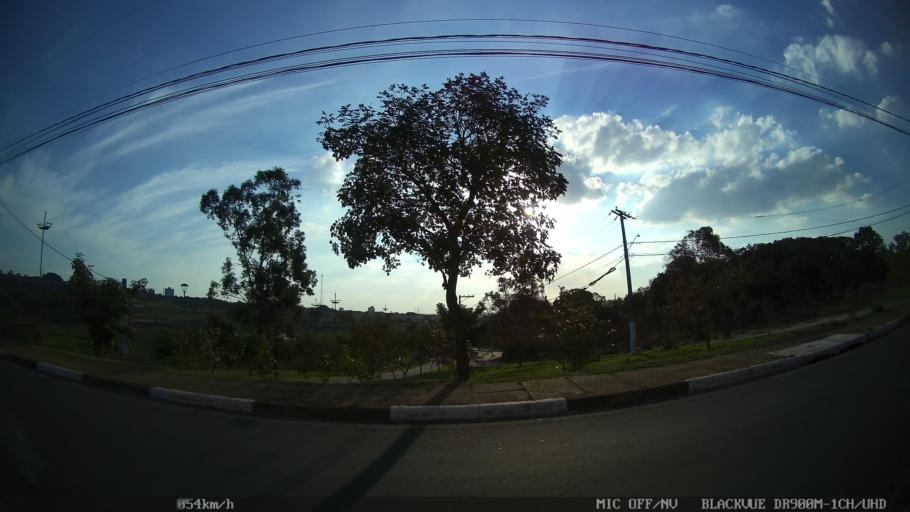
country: BR
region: Sao Paulo
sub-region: Hortolandia
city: Hortolandia
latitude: -22.8710
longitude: -47.1932
